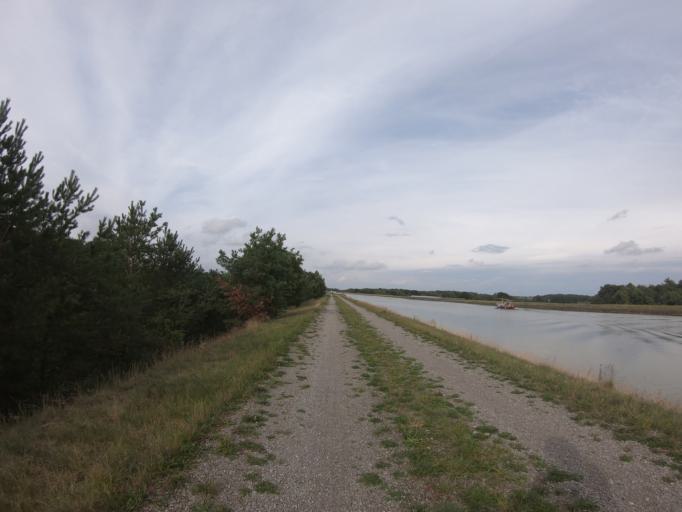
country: DE
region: Lower Saxony
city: Osloss
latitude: 52.4667
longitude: 10.6553
